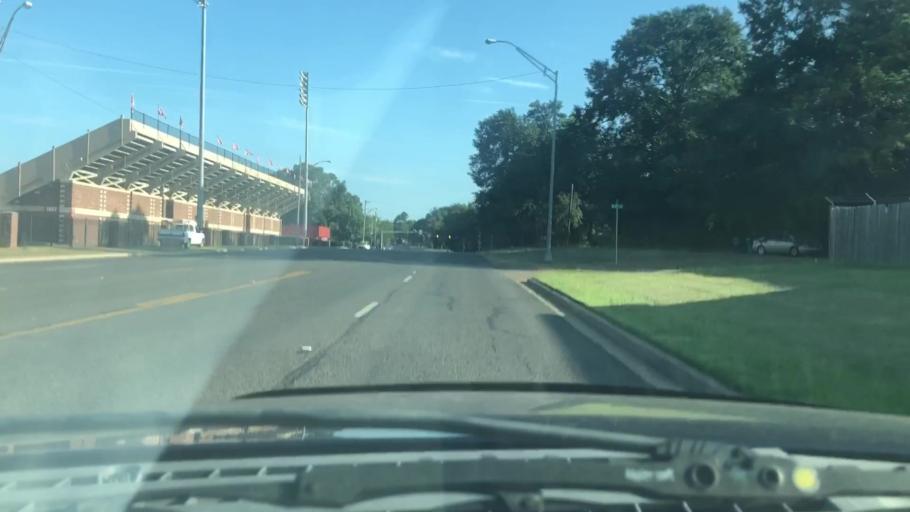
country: US
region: Texas
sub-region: Bowie County
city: Texarkana
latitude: 33.4270
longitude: -94.0614
